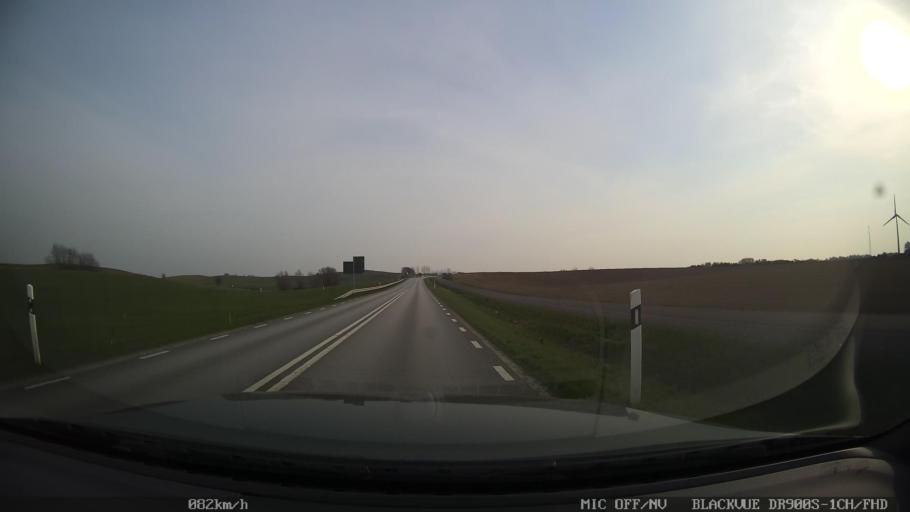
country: SE
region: Skane
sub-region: Ystads Kommun
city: Ystad
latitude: 55.4661
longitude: 13.7992
